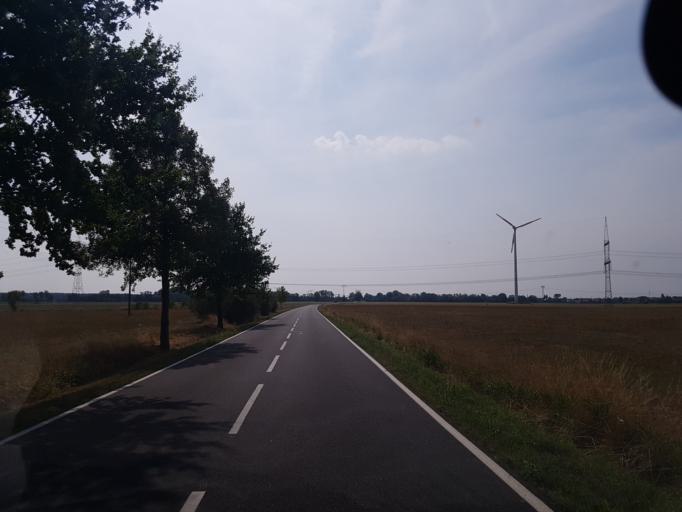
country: DE
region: Brandenburg
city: Finsterwalde
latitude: 51.6556
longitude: 13.7345
